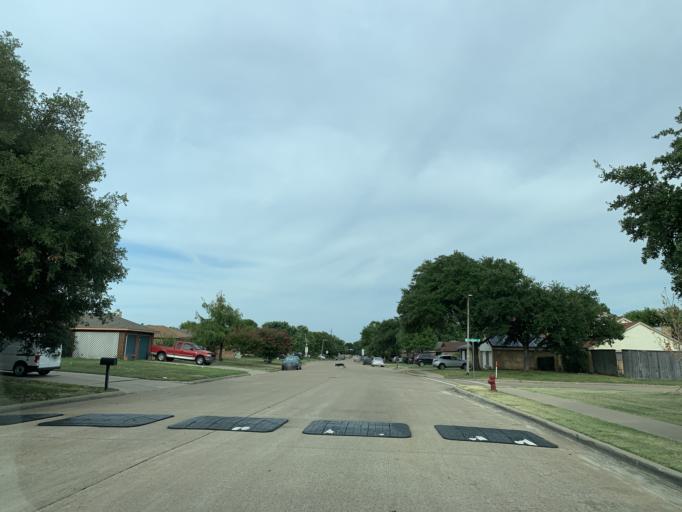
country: US
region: Texas
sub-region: Tarrant County
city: Arlington
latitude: 32.6624
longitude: -97.0461
